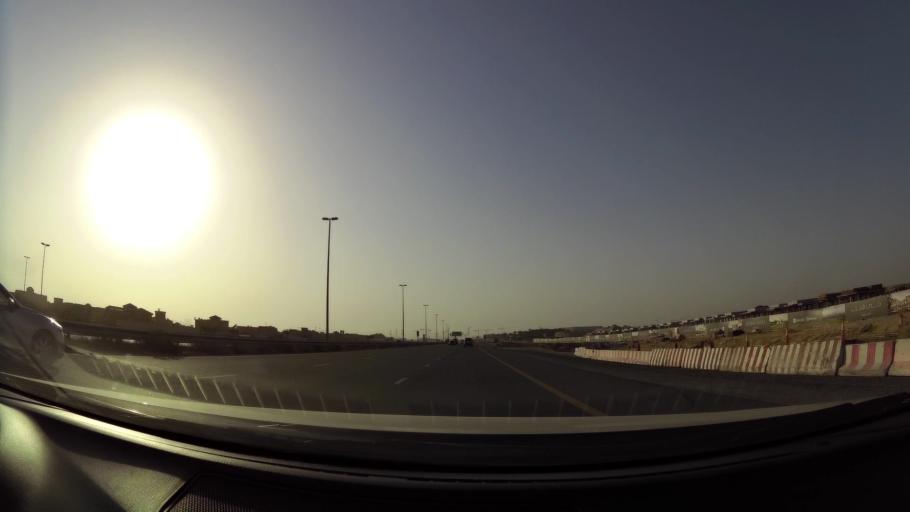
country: AE
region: Dubai
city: Dubai
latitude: 25.0886
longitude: 55.2472
